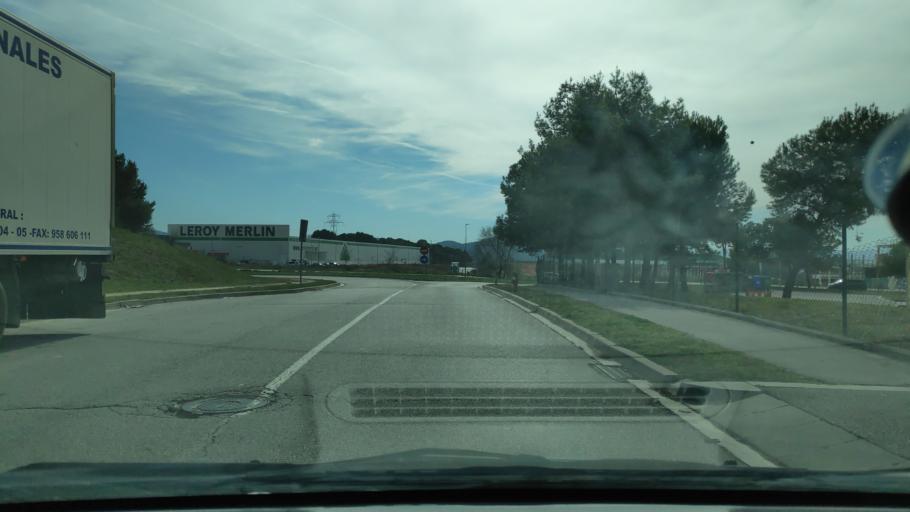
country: ES
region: Catalonia
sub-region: Provincia de Barcelona
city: Rubi
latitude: 41.4847
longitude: 2.0457
